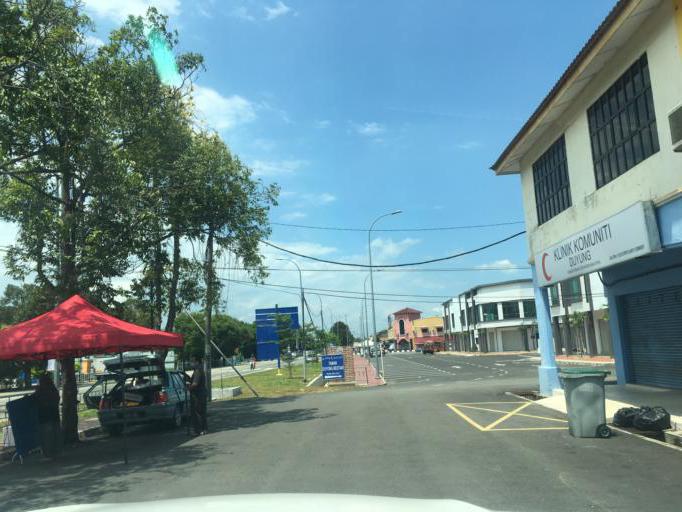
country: MY
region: Melaka
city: Kampung Ayer Molek
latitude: 2.2033
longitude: 102.3078
